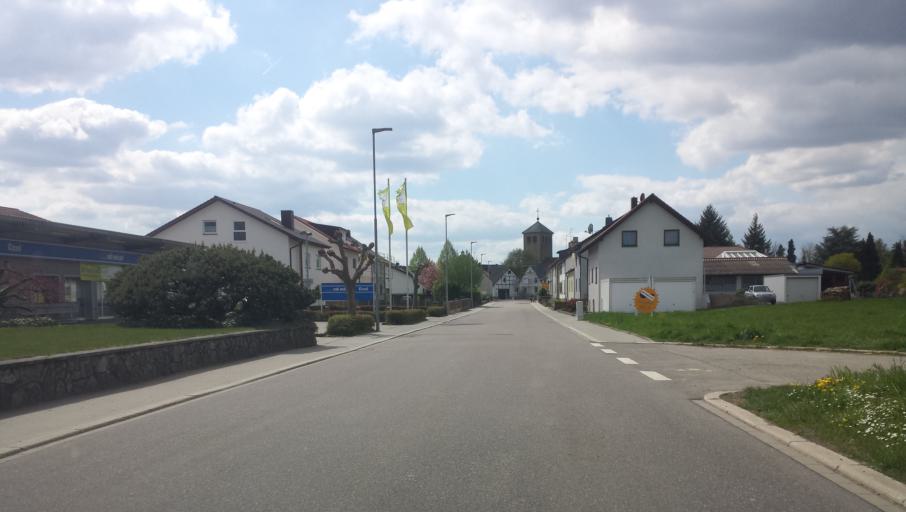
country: DE
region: Baden-Wuerttemberg
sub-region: Karlsruhe Region
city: Sinsheim
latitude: 49.1974
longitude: 8.8644
